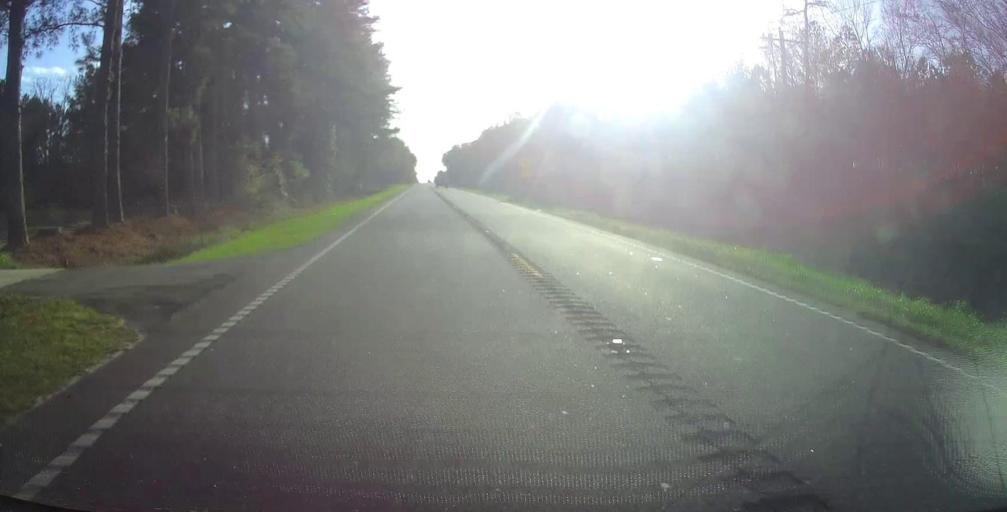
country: US
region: Georgia
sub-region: Tattnall County
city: Reidsville
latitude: 32.1248
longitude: -82.0605
